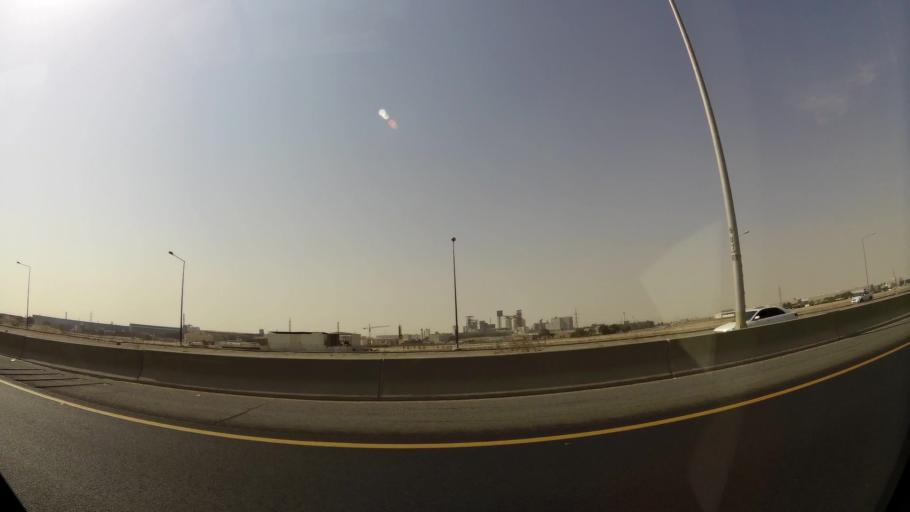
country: KW
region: Al Ahmadi
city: Al Fahahil
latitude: 29.0056
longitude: 48.1357
